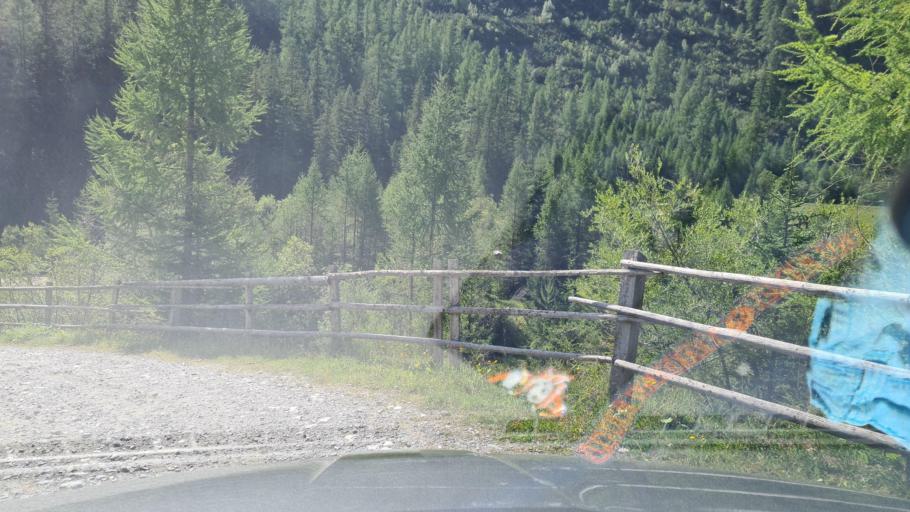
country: AT
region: Salzburg
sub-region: Politischer Bezirk Tamsweg
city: Zederhaus
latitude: 47.1869
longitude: 13.4034
